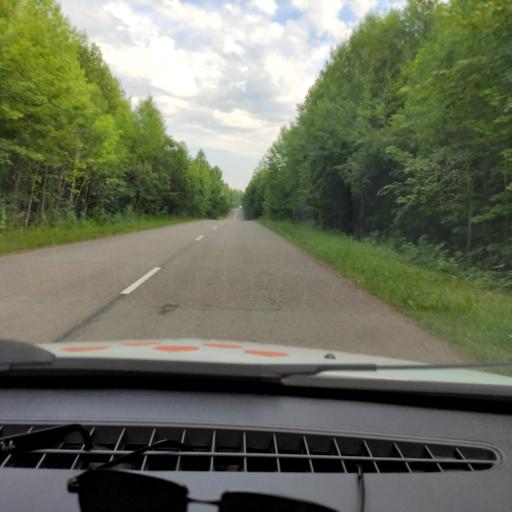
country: RU
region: Bashkortostan
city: Chishmy
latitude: 54.4427
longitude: 55.5565
